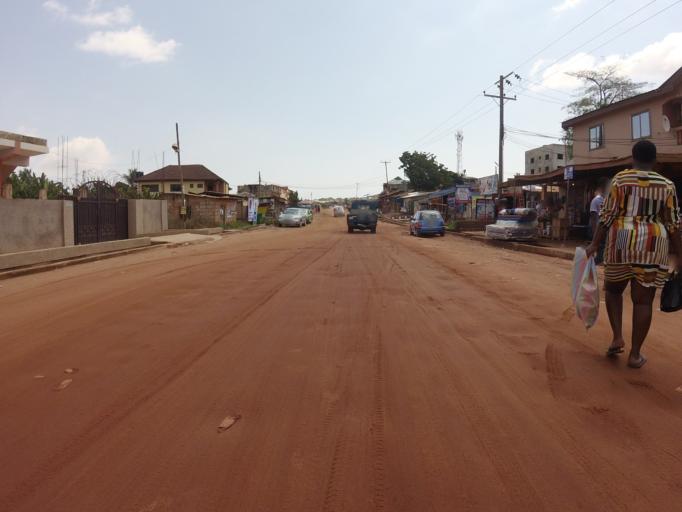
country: GH
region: Greater Accra
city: Gbawe
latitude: 5.6243
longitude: -0.3064
